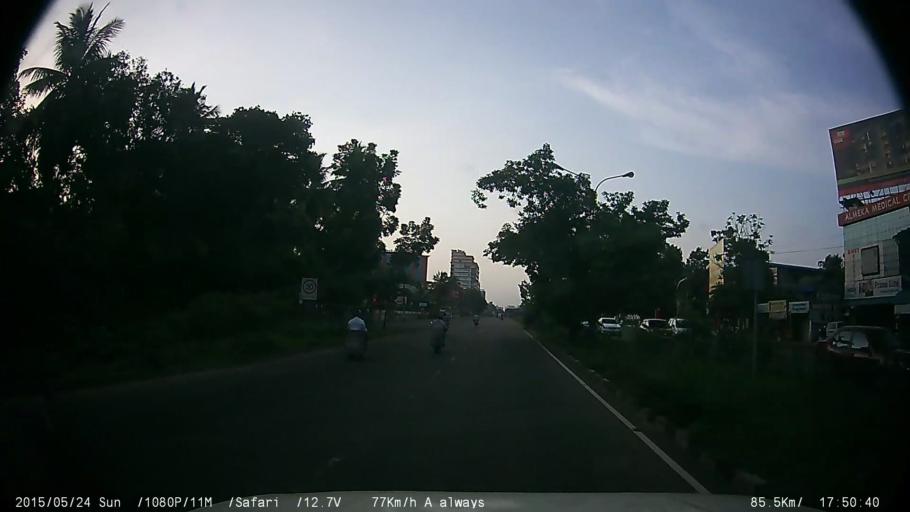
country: IN
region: Kerala
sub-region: Ernakulam
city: Elur
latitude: 10.0008
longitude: 76.3137
